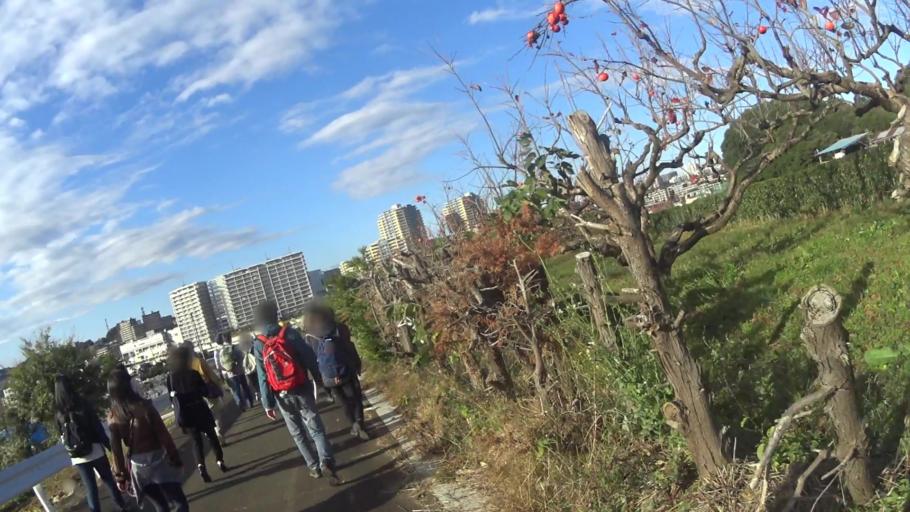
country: JP
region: Tokyo
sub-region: Machida-shi
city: Machida
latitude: 35.6168
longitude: 139.4763
